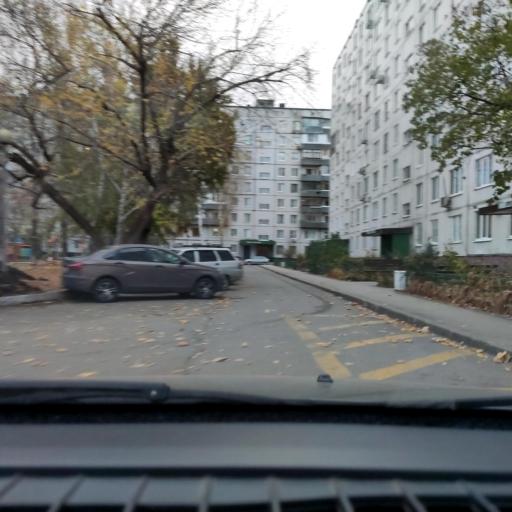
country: RU
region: Samara
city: Tol'yatti
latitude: 53.5072
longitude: 49.2785
